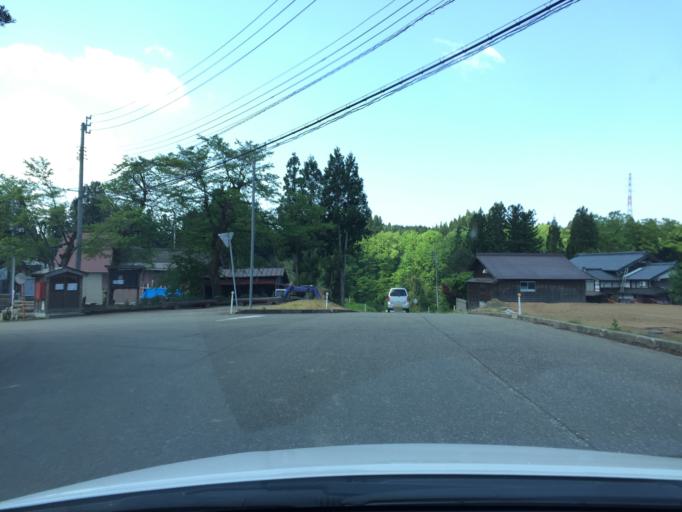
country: JP
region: Niigata
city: Tochio-honcho
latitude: 37.4761
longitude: 139.0434
